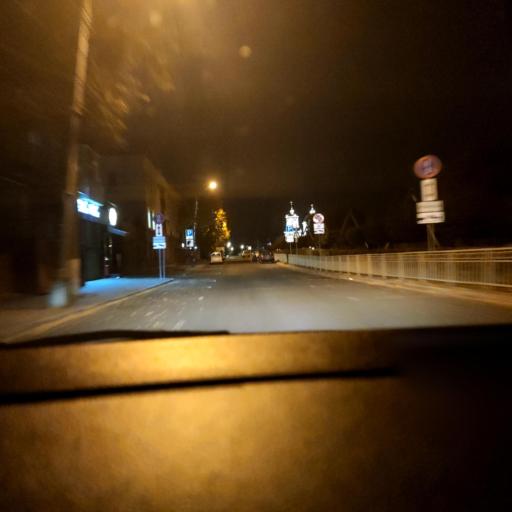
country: RU
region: Voronezj
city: Voronezh
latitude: 51.6631
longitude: 39.2099
